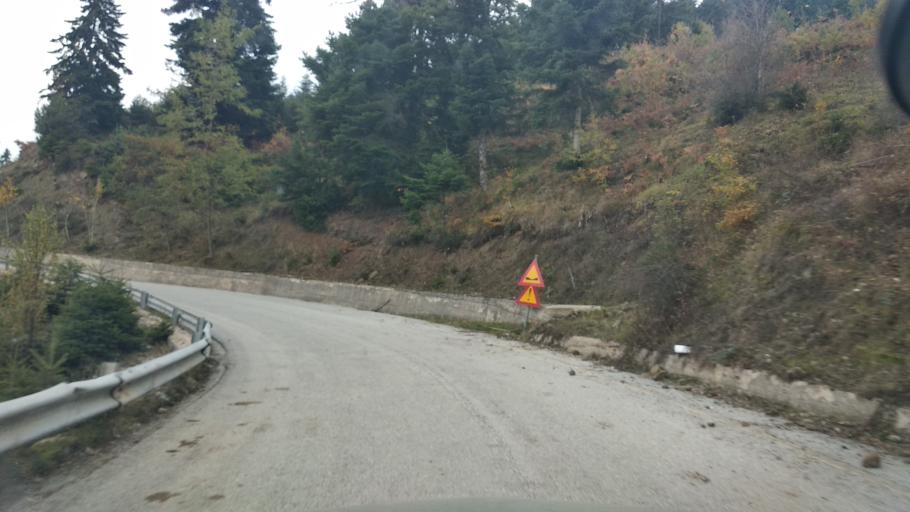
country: GR
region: Thessaly
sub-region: Trikala
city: Kalampaka
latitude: 39.5878
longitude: 21.4911
